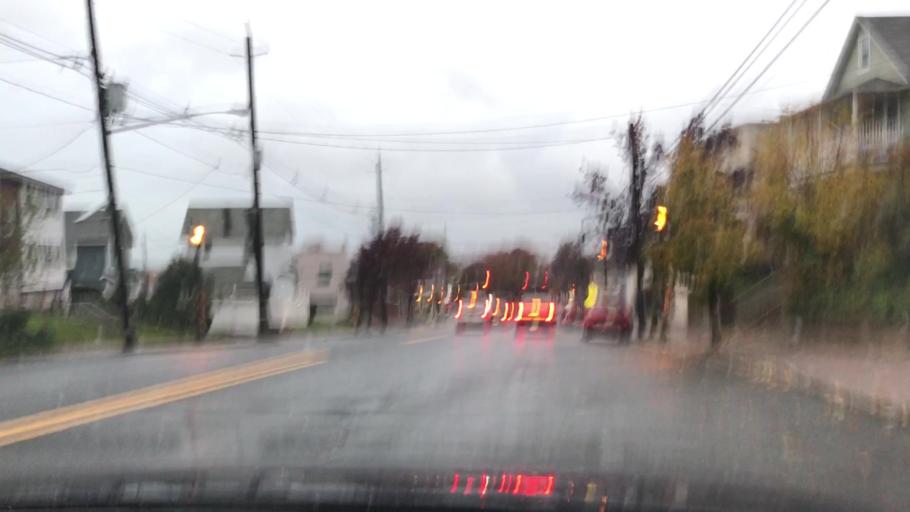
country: US
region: New Jersey
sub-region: Bergen County
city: Bogota
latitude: 40.8764
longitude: -74.0236
